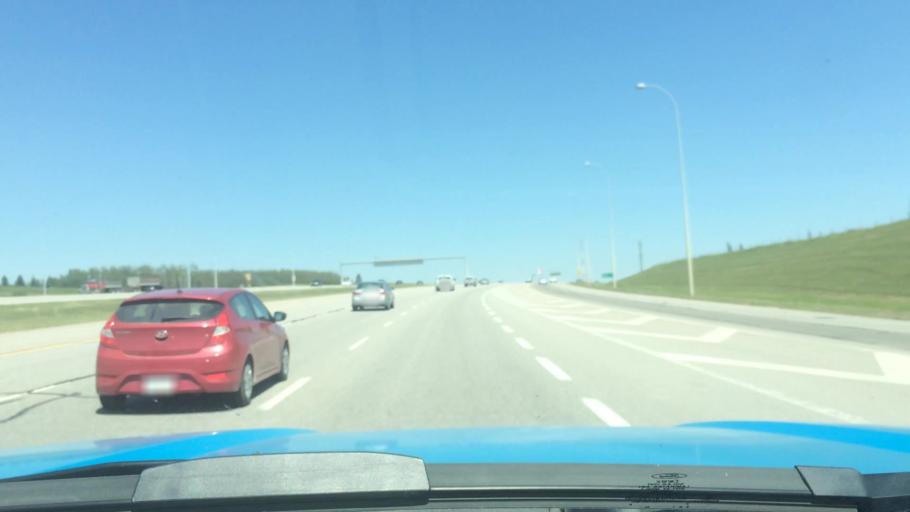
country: CA
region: Alberta
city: Calgary
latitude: 51.1466
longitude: -114.2009
